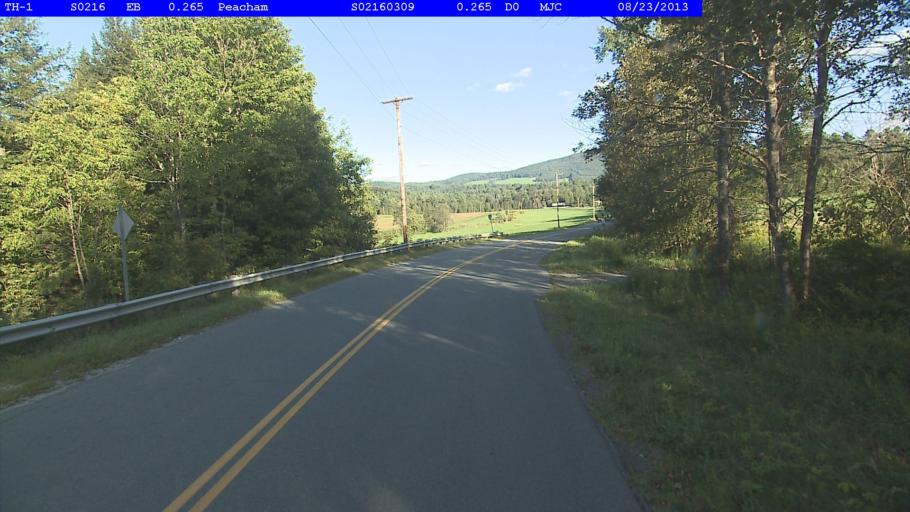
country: US
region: Vermont
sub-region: Caledonia County
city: Saint Johnsbury
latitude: 44.3135
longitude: -72.1614
